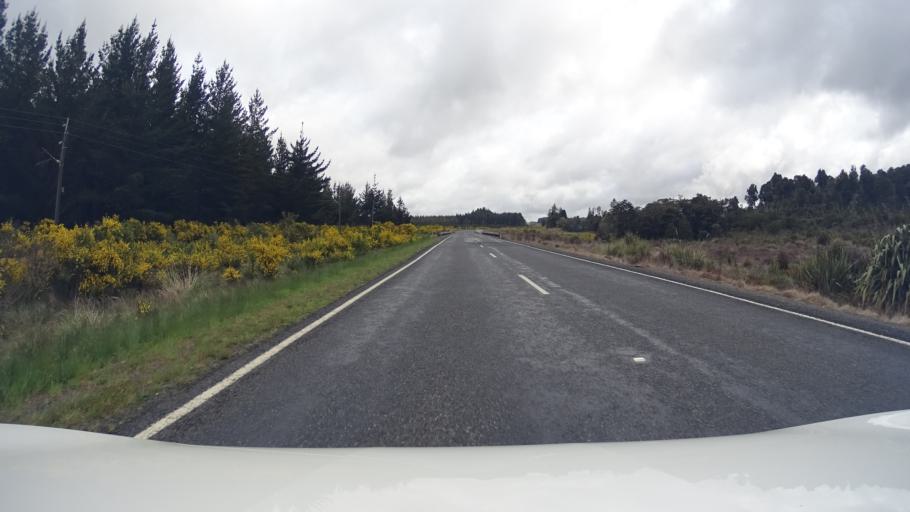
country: NZ
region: Manawatu-Wanganui
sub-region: Ruapehu District
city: Waiouru
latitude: -39.2188
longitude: 175.4006
